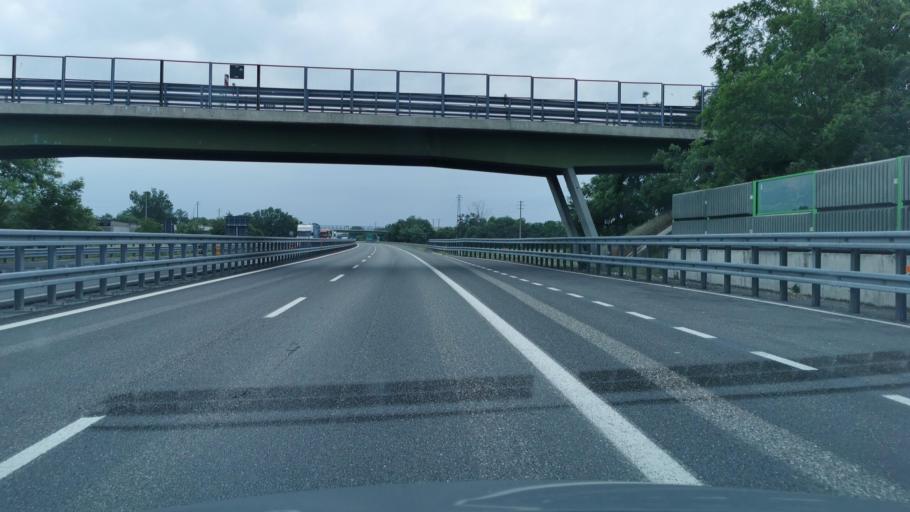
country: IT
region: Lombardy
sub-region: Provincia di Pavia
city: Stradella
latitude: 45.0829
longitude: 9.2928
